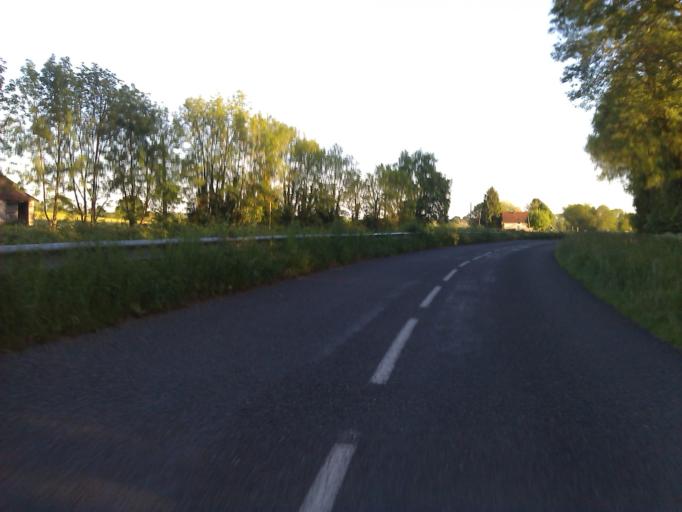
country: FR
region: Bourgogne
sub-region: Departement de Saone-et-Loire
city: Palinges
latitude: 46.5054
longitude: 4.1860
